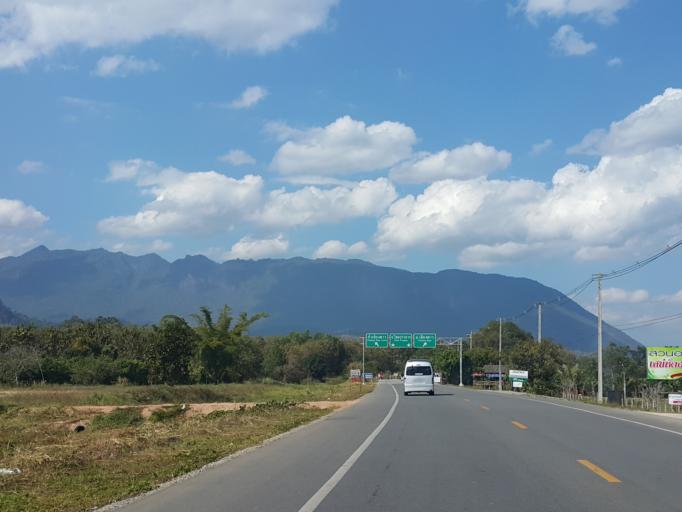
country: TH
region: Chiang Mai
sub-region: Amphoe Chiang Dao
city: Chiang Dao
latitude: 19.3718
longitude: 98.9479
